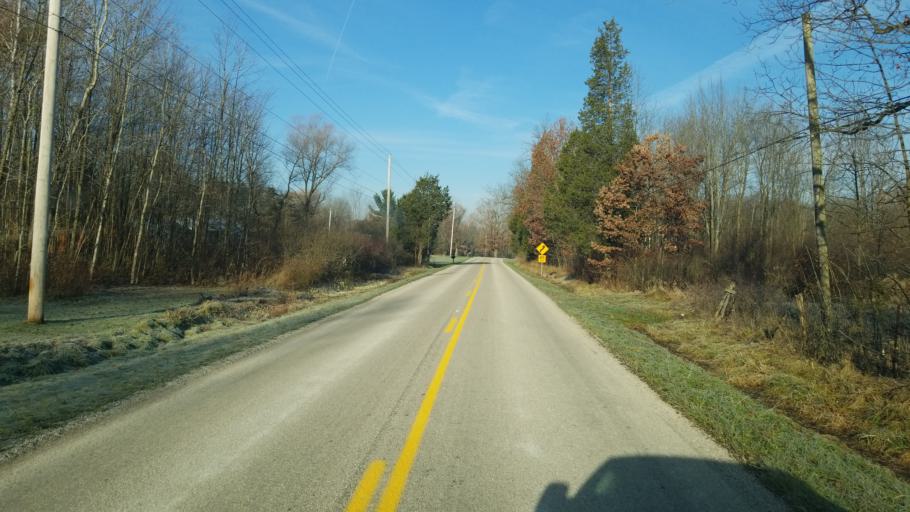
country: US
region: Ohio
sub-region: Ashtabula County
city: Andover
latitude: 41.6719
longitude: -80.6600
